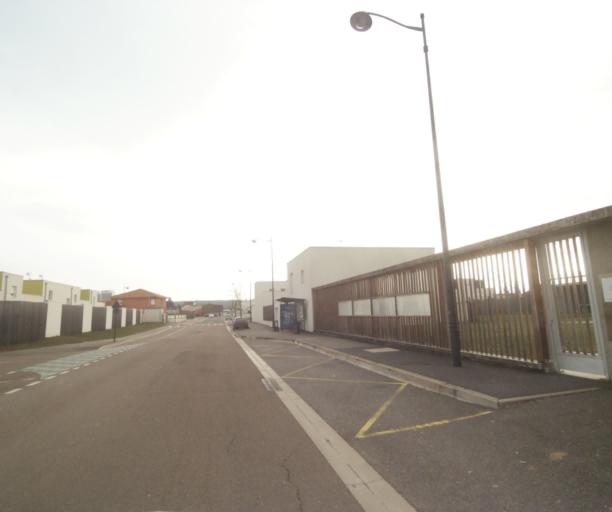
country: FR
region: Champagne-Ardenne
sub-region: Departement de la Haute-Marne
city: Bettancourt-la-Ferree
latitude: 48.6378
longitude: 4.9673
